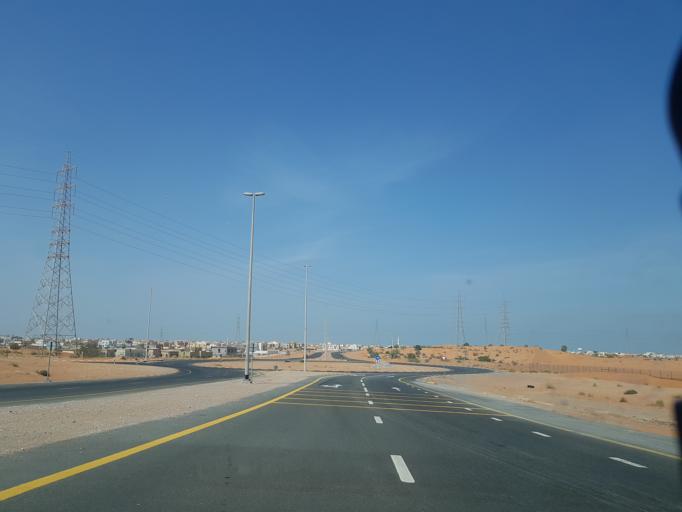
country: AE
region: Ra's al Khaymah
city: Ras al-Khaimah
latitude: 25.6973
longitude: 55.9227
